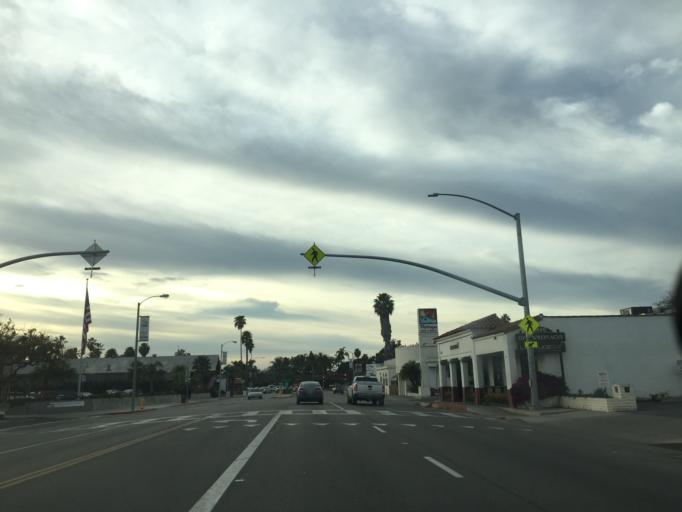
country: US
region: California
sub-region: Santa Barbara County
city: Goleta
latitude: 34.4360
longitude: -119.8283
